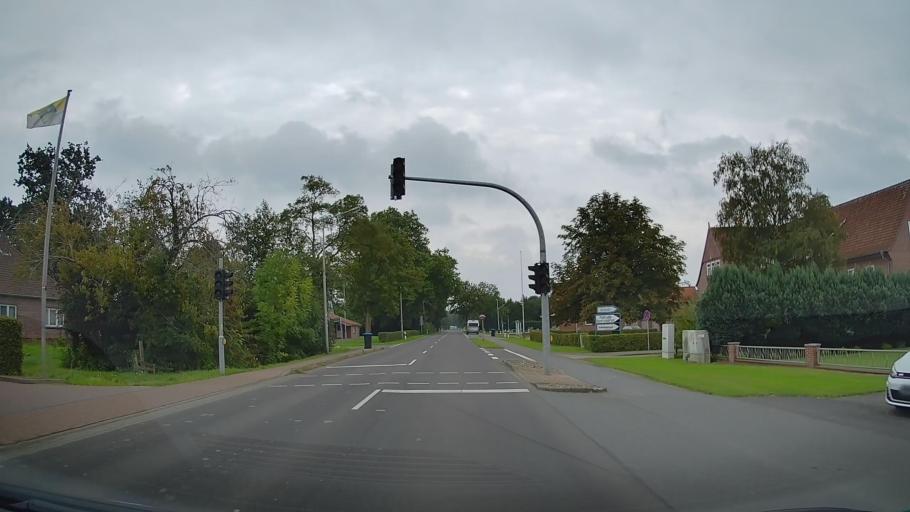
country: DE
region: Lower Saxony
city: Drochtersen
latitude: 53.7340
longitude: 9.3469
